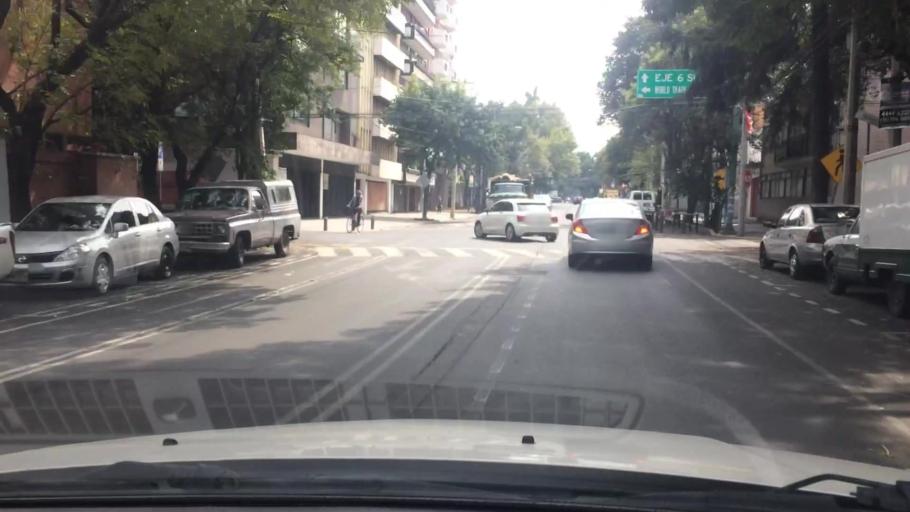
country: MX
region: Mexico City
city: Colonia del Valle
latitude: 19.3918
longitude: -99.1792
